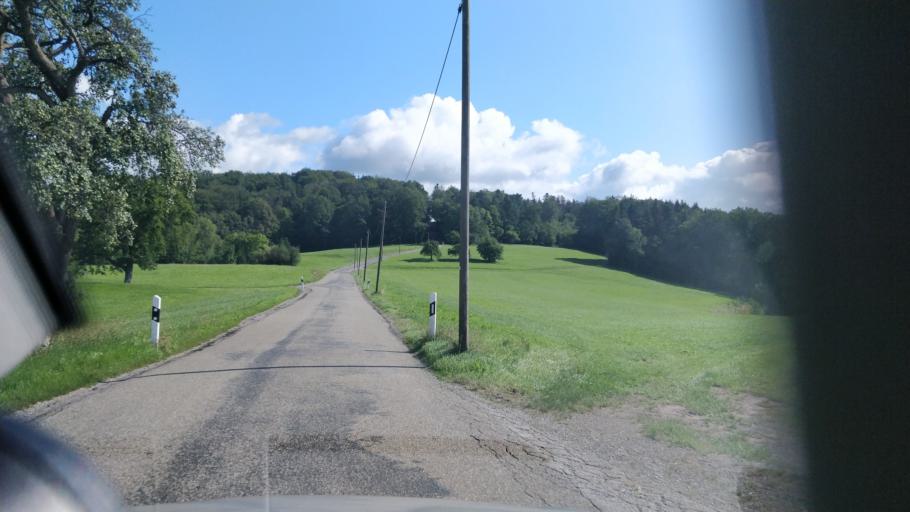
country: DE
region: Baden-Wuerttemberg
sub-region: Regierungsbezirk Stuttgart
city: Murrhardt
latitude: 49.0159
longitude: 9.5954
